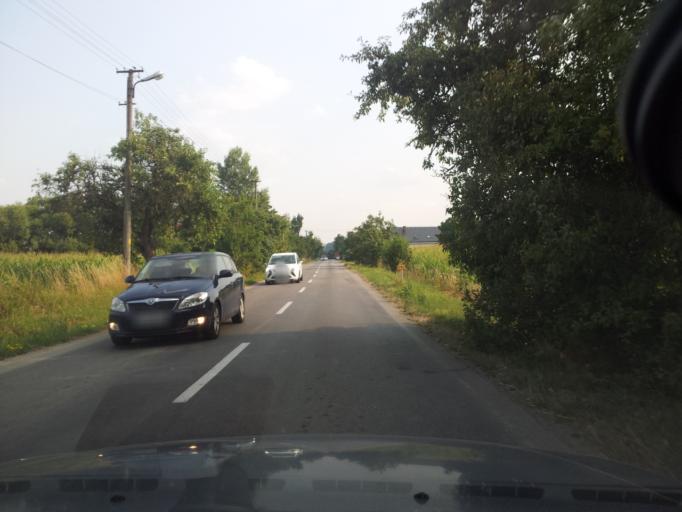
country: SK
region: Nitriansky
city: Banovce nad Bebravou
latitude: 48.7861
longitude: 18.1987
